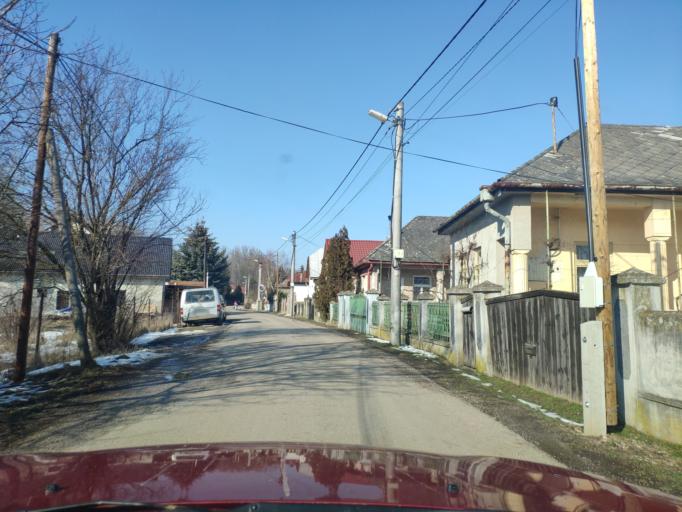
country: HU
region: Borsod-Abauj-Zemplen
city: Gonc
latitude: 48.5812
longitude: 21.2729
